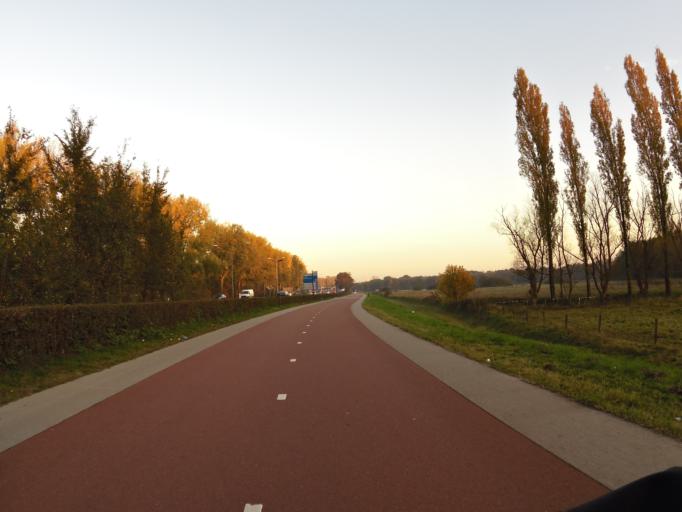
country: NL
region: North Brabant
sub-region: Gemeente 's-Hertogenbosch
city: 's-Hertogenbosch
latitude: 51.6932
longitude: 5.2535
